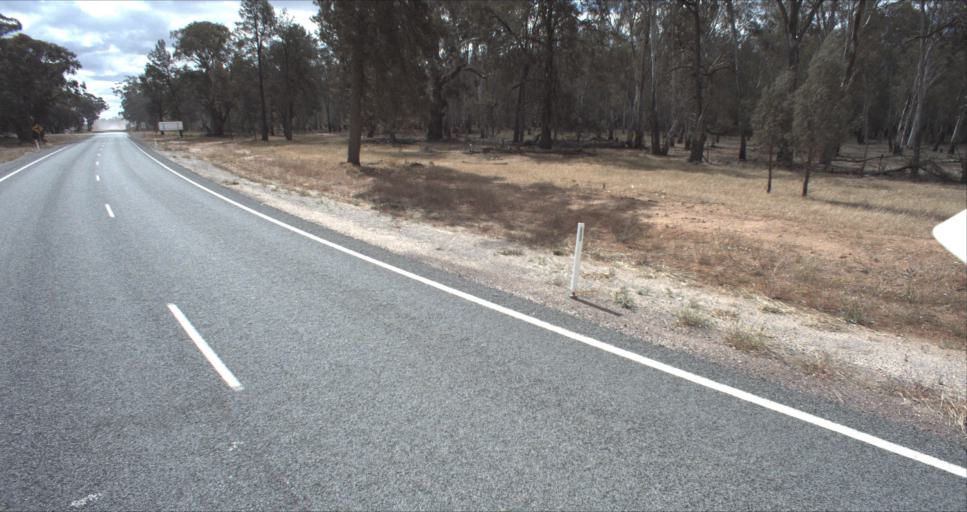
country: AU
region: New South Wales
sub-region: Leeton
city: Leeton
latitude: -34.6437
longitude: 146.3552
